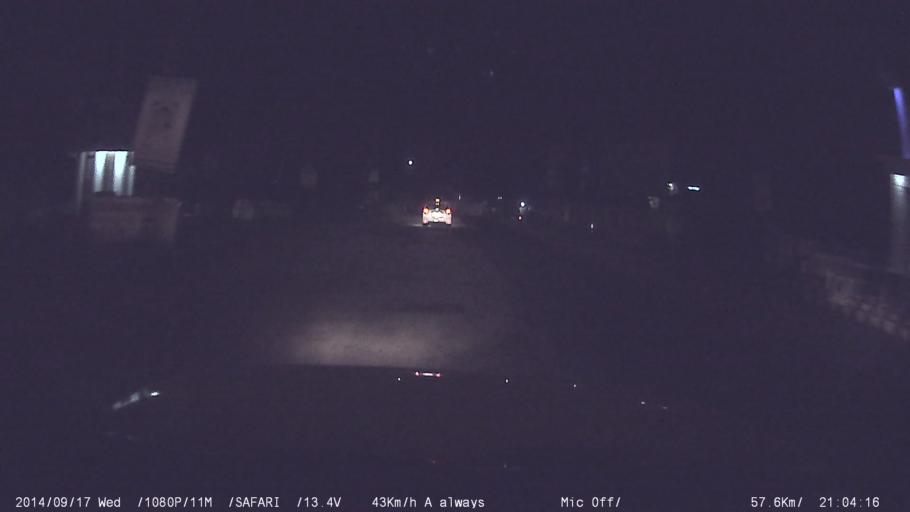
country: IN
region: Kerala
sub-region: Kottayam
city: Changanacheri
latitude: 9.4956
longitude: 76.5245
